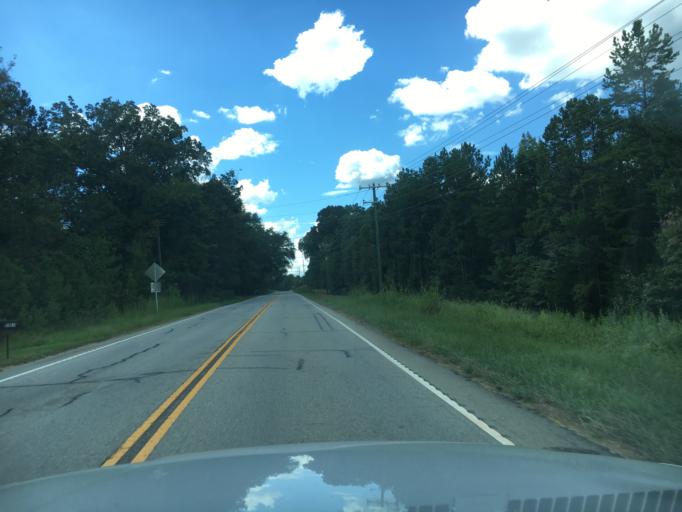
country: US
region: South Carolina
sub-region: Laurens County
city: Laurens
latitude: 34.5218
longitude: -82.1442
